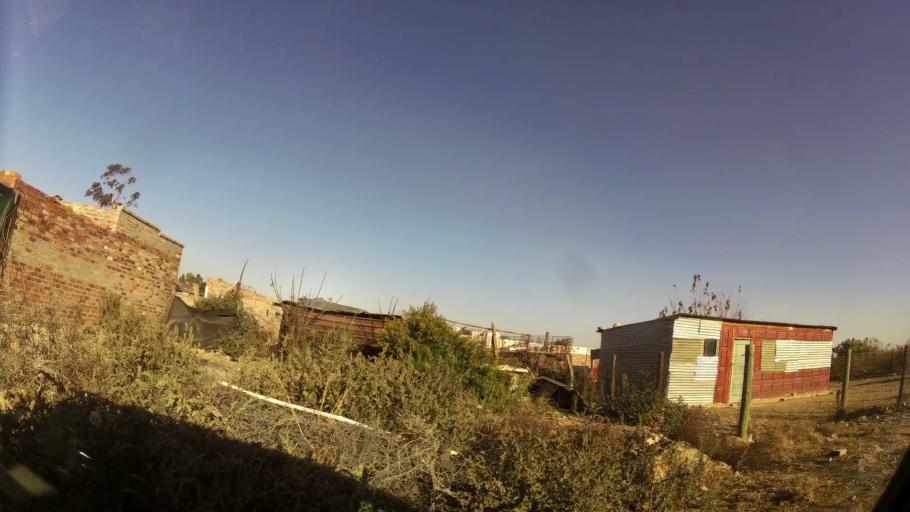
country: ZA
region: Gauteng
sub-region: City of Johannesburg Metropolitan Municipality
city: Diepsloot
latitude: -25.9284
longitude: 28.0120
